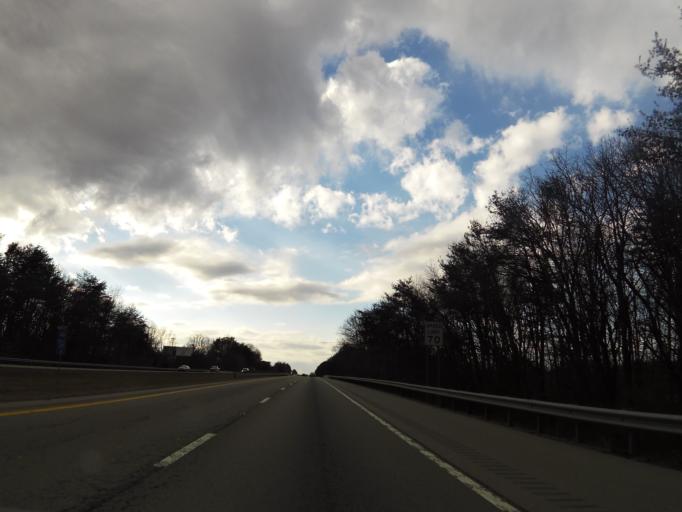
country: US
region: Tennessee
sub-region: Cumberland County
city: Fairfield Glade
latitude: 35.9110
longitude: -84.8871
